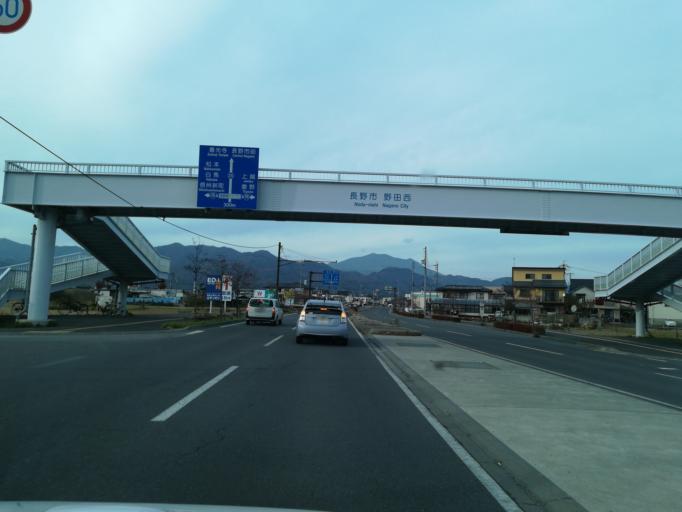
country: JP
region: Nagano
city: Nagano-shi
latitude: 36.6011
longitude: 138.1799
